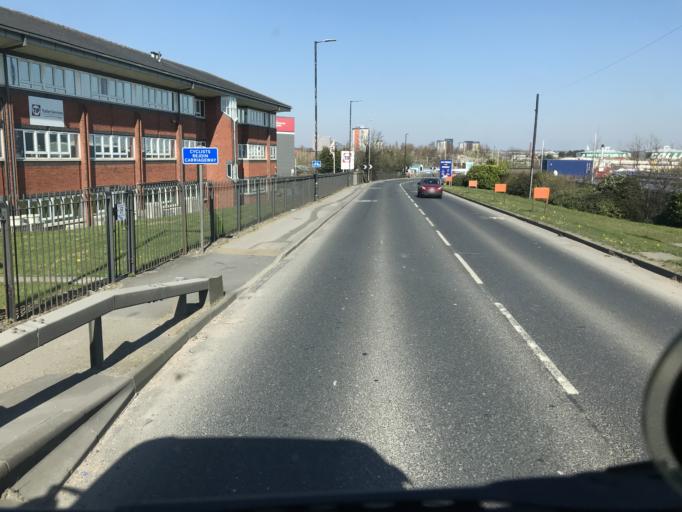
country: GB
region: England
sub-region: City and Borough of Salford
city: Eccles
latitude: 53.4728
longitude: -2.3472
